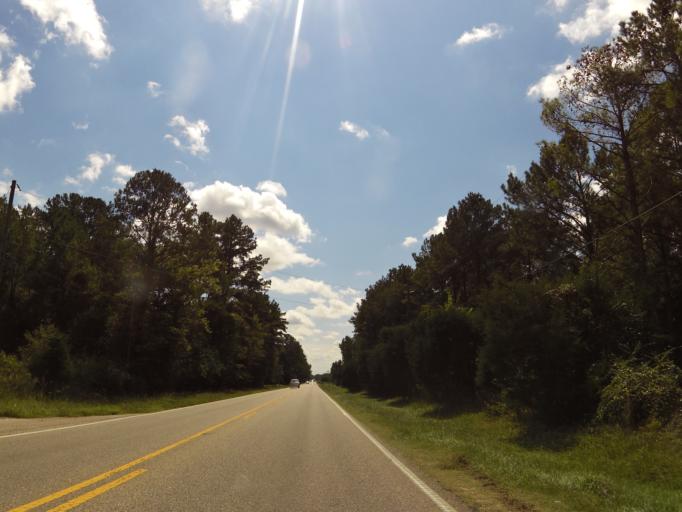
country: US
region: Alabama
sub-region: Dallas County
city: Selma
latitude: 32.4347
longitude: -87.0835
